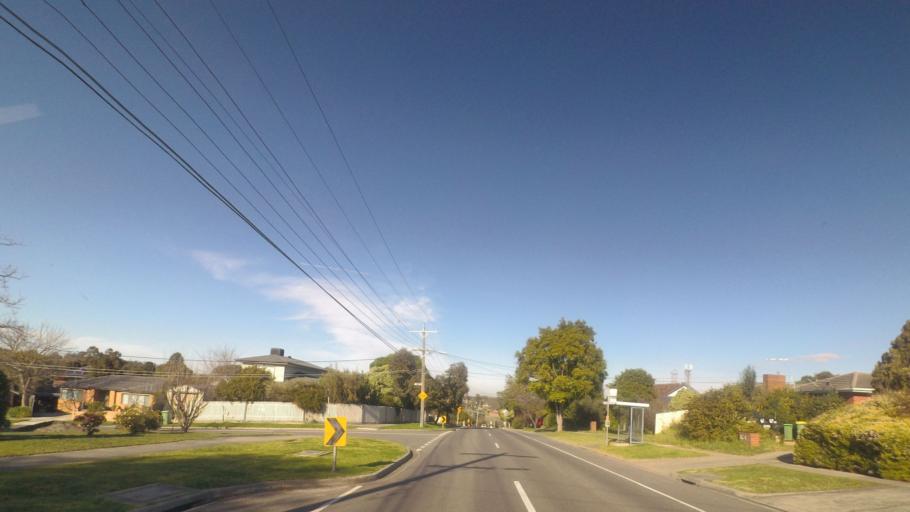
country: AU
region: Victoria
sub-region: Banyule
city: Yallambie
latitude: -37.7234
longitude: 145.1044
